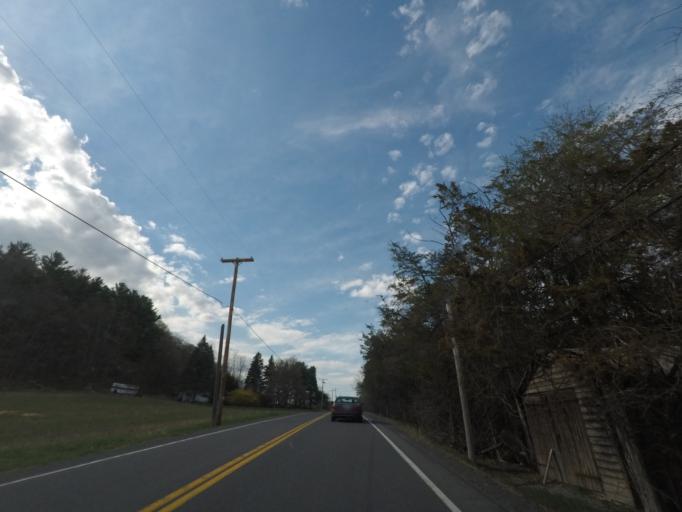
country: US
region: New York
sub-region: Albany County
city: Voorheesville
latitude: 42.5631
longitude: -73.9519
